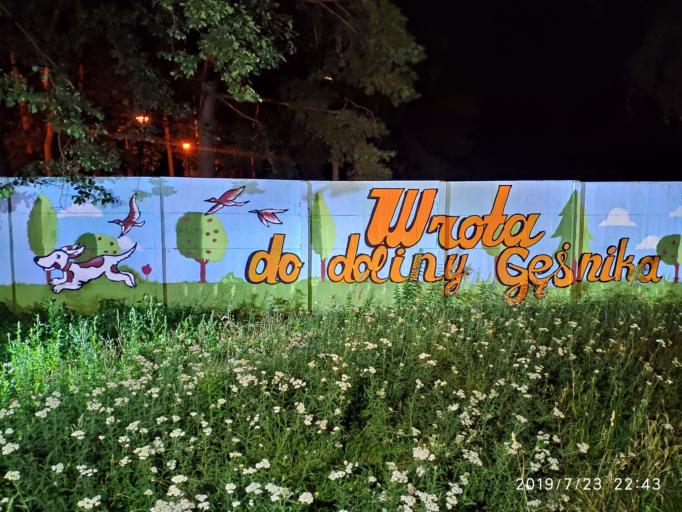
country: PL
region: Lubusz
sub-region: Zielona Gora
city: Zielona Gora
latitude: 51.9580
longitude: 15.4998
